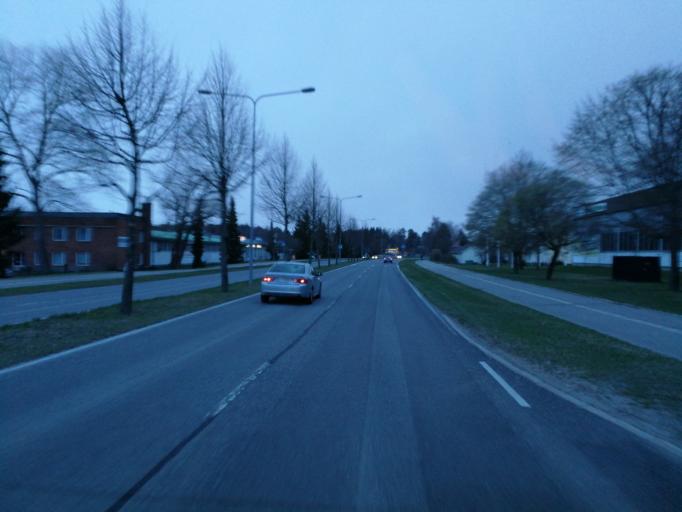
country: FI
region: Varsinais-Suomi
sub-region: Turku
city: Turku
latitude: 60.4683
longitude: 22.2420
